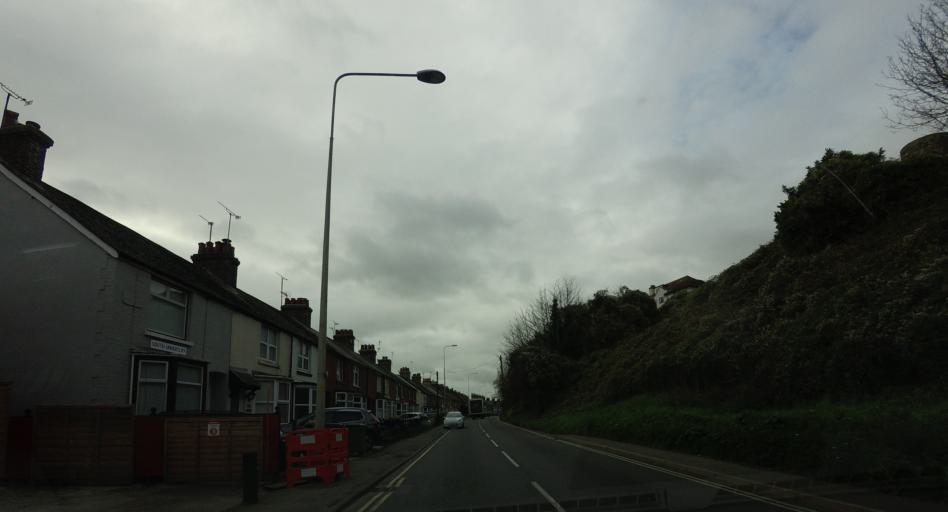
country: GB
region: England
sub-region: East Sussex
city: Rye
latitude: 50.9495
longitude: 0.7362
